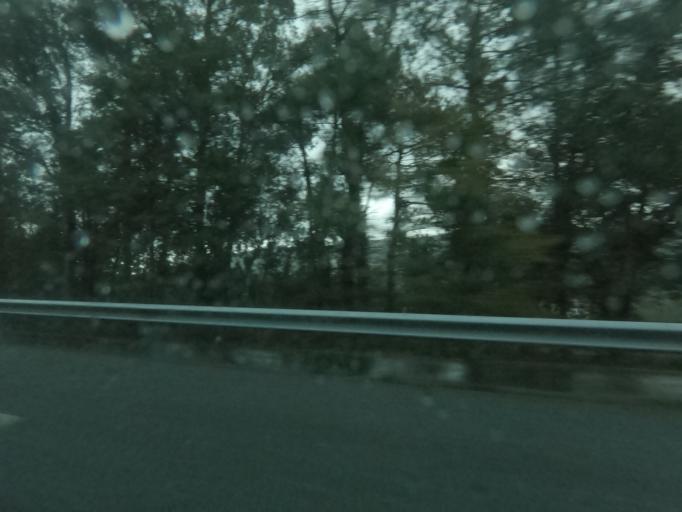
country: ES
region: Galicia
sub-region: Provincia de Pontevedra
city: Pontevedra
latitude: 42.3776
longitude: -8.6362
